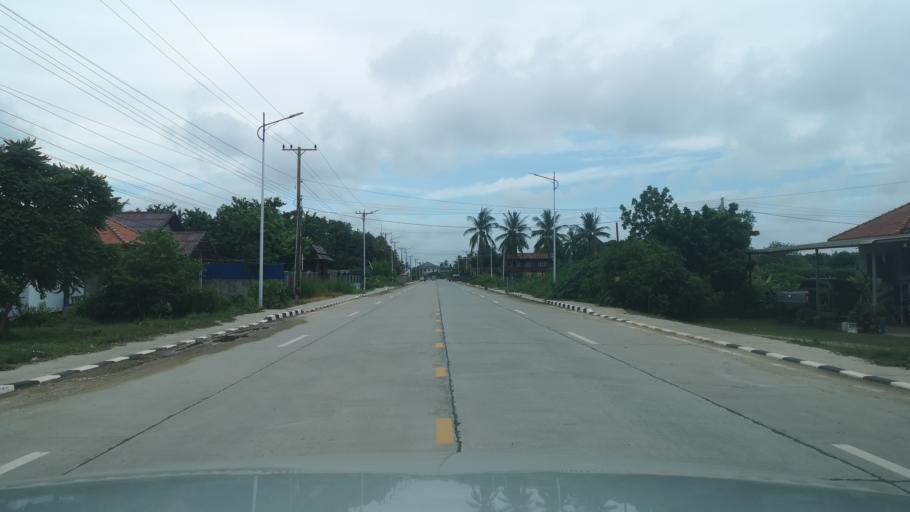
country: TH
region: Nong Khai
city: Tha Bo
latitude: 17.8239
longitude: 102.6604
